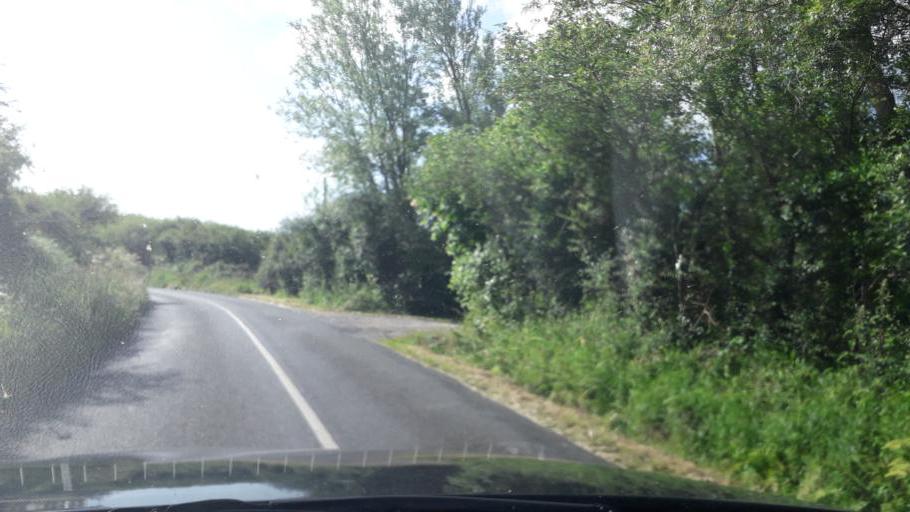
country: IE
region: Leinster
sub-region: Loch Garman
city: Loch Garman
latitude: 52.2580
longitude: -6.5540
